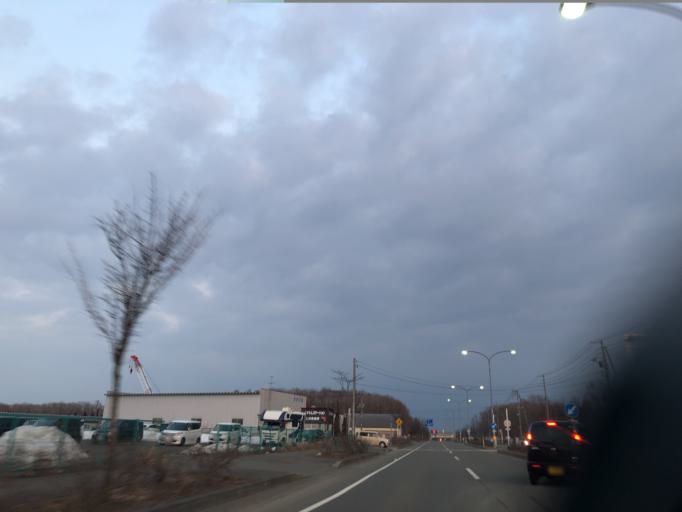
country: JP
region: Hokkaido
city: Chitose
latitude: 42.8207
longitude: 141.6748
